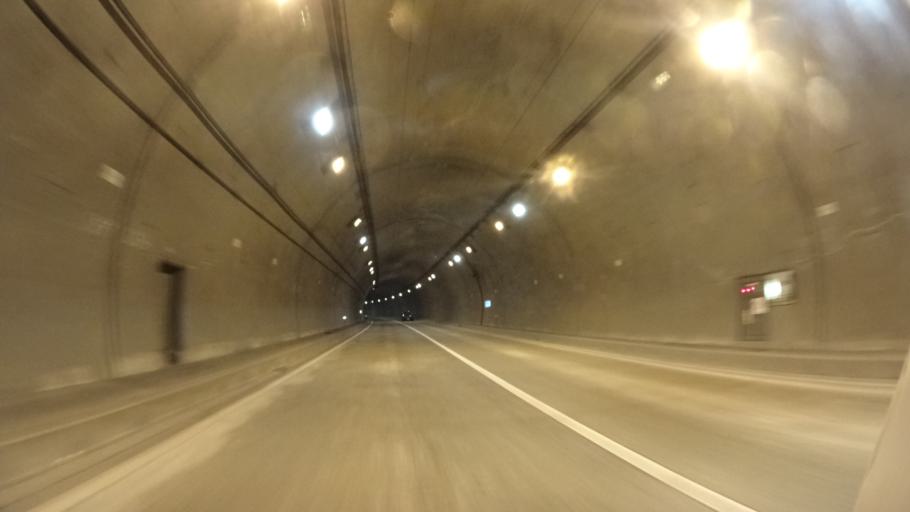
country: JP
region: Fukui
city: Tsuruga
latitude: 35.6166
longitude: 136.0837
